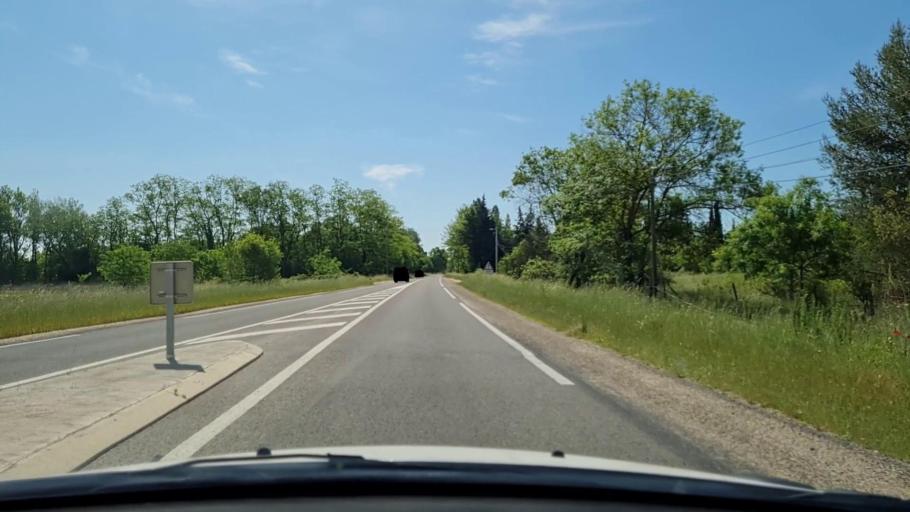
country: FR
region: Languedoc-Roussillon
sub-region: Departement du Gard
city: Saint-Genies-de-Malgoires
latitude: 43.9565
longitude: 4.2420
